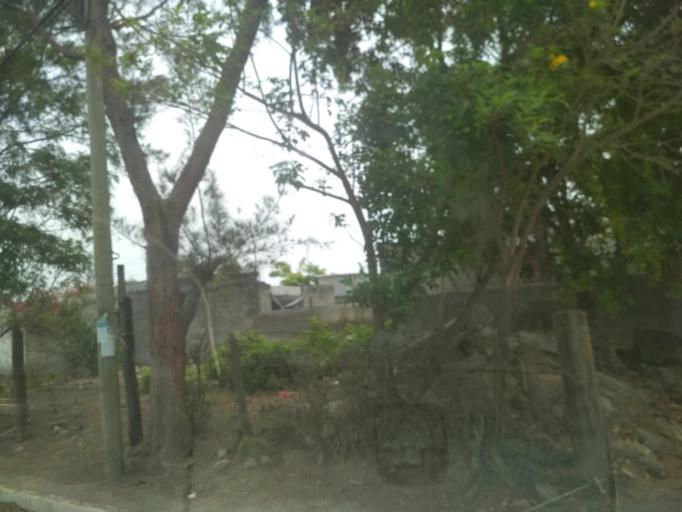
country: MX
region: Veracruz
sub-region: Veracruz
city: Rio Medio [Granja]
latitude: 19.2113
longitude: -96.2089
